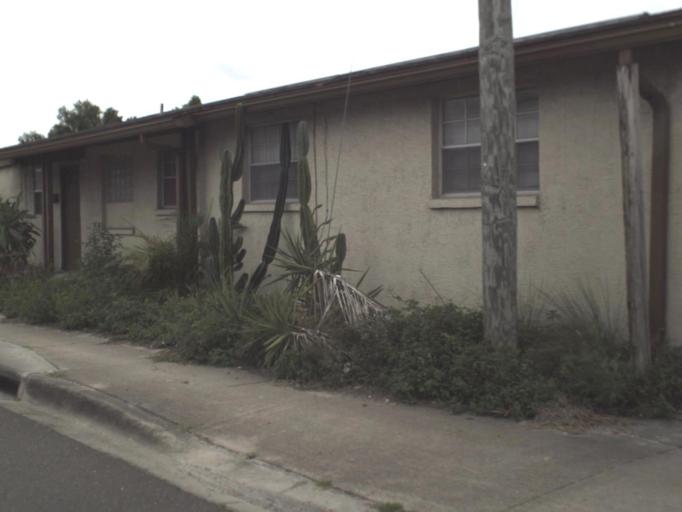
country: US
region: Florida
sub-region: Pasco County
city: Elfers
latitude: 28.2169
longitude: -82.7308
